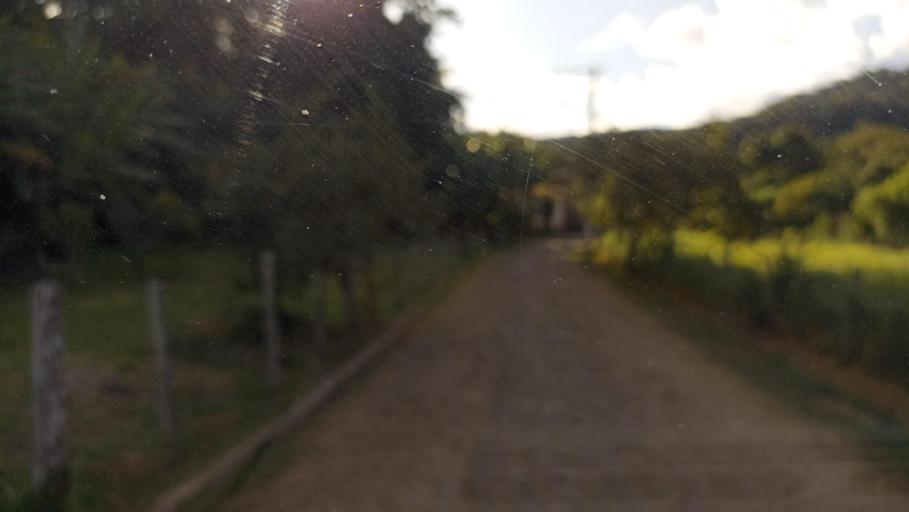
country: BR
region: Minas Gerais
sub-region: Ouro Preto
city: Ouro Preto
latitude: -20.3129
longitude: -43.5787
